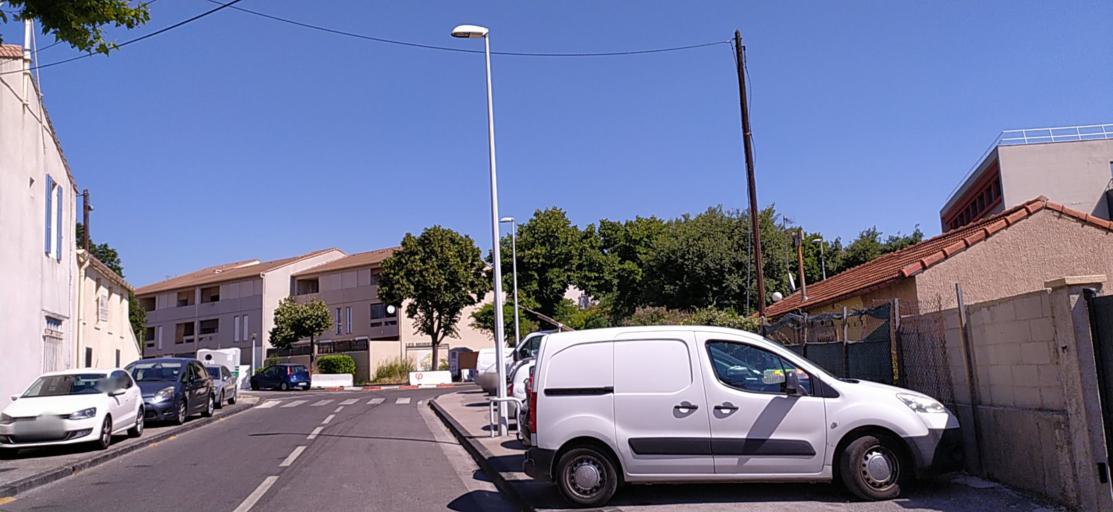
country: FR
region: Provence-Alpes-Cote d'Azur
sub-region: Departement des Bouches-du-Rhone
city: Marseille 16
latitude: 43.3589
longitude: 5.3353
